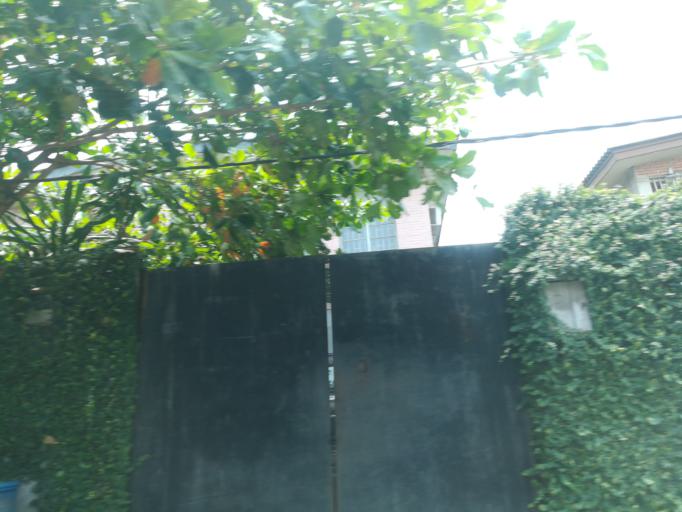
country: NG
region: Lagos
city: Somolu
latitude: 6.5493
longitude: 3.3601
